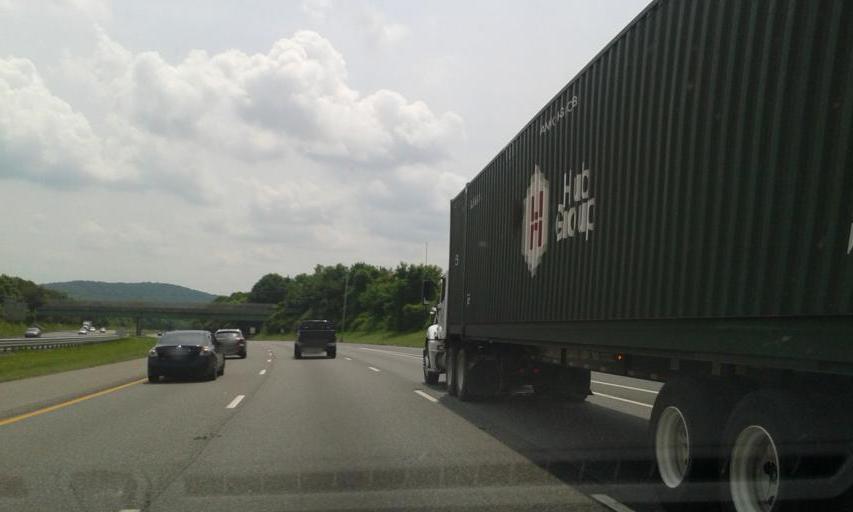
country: US
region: New Jersey
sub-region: Warren County
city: Alpha
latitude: 40.6671
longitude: -75.1397
